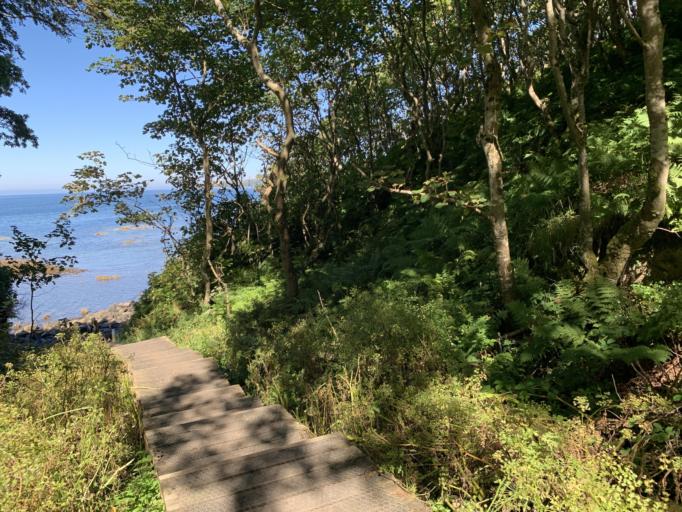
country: GB
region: Scotland
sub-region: South Ayrshire
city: Maybole
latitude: 55.3523
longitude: -4.7950
